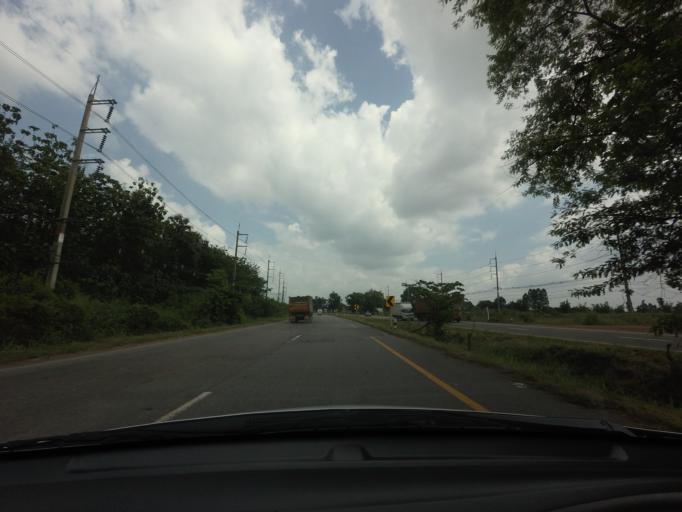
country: TH
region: Prachin Buri
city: Kabin Buri
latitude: 13.9052
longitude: 101.6591
